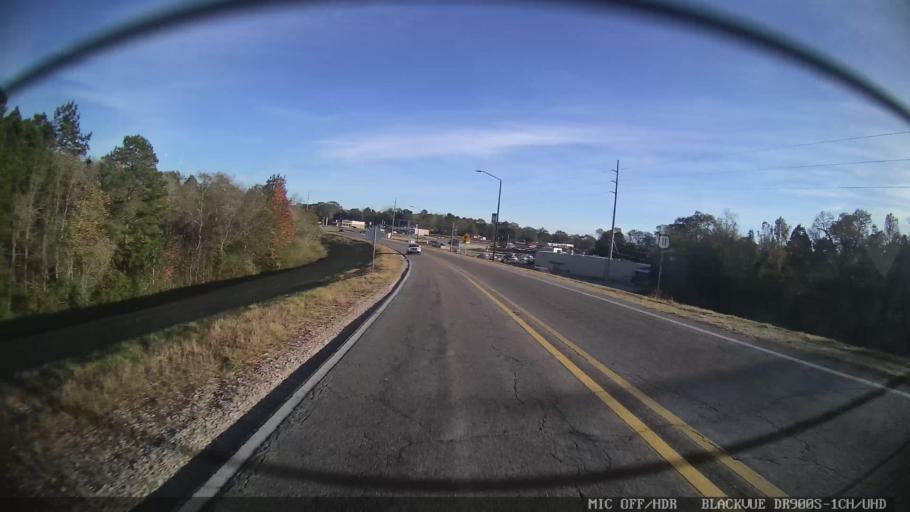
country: US
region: Mississippi
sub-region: Lamar County
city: Purvis
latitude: 31.1480
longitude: -89.4056
